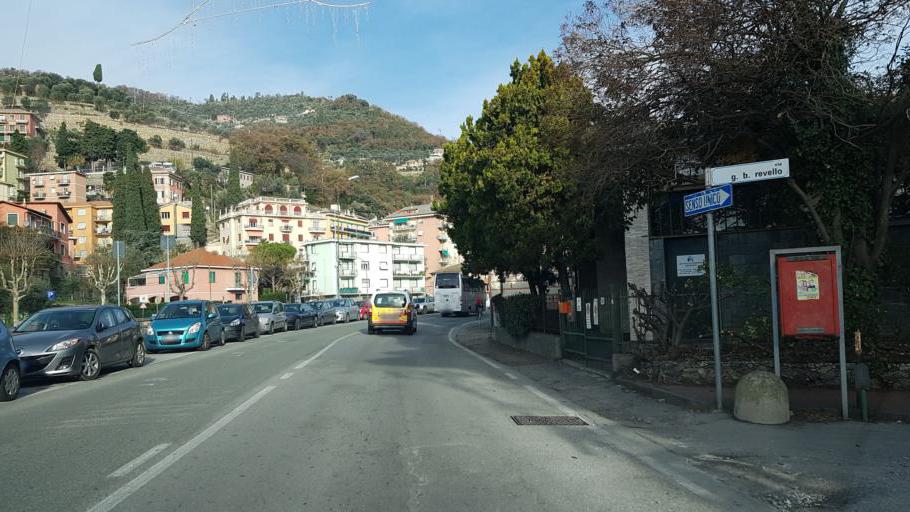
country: IT
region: Liguria
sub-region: Provincia di Genova
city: Recco
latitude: 44.3666
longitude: 9.1466
